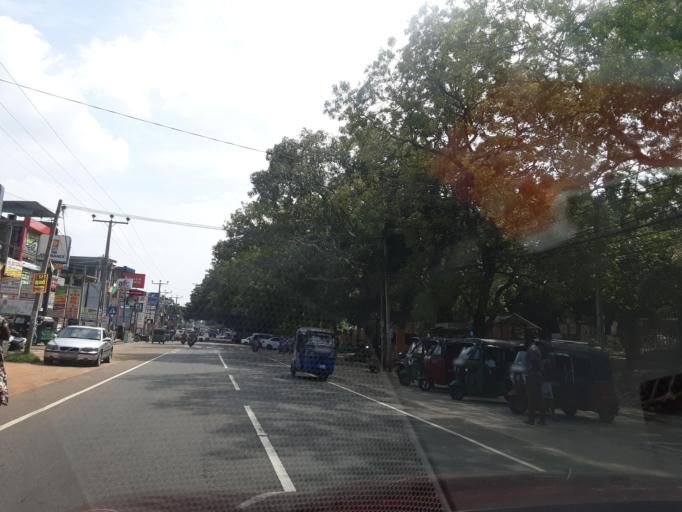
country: LK
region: Northern Province
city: Vavuniya
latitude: 8.5417
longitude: 80.4916
